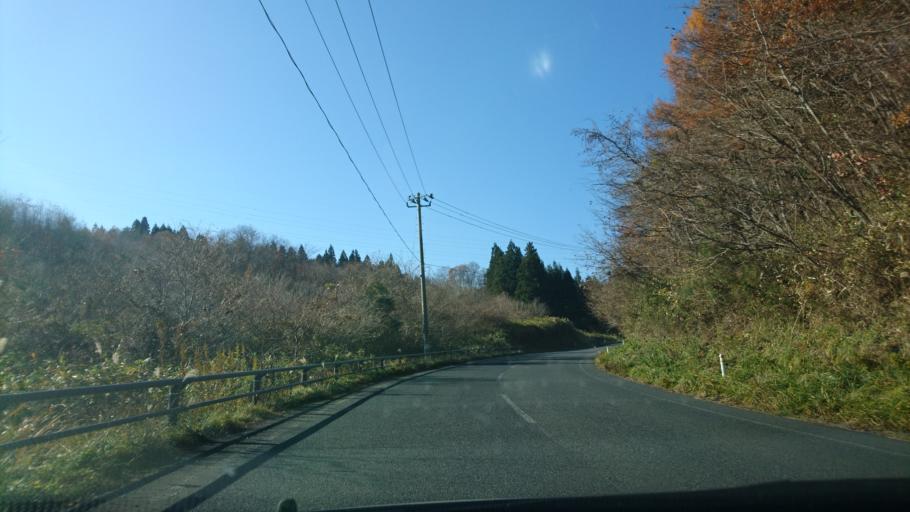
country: JP
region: Iwate
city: Ichinoseki
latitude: 38.9031
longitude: 141.4130
